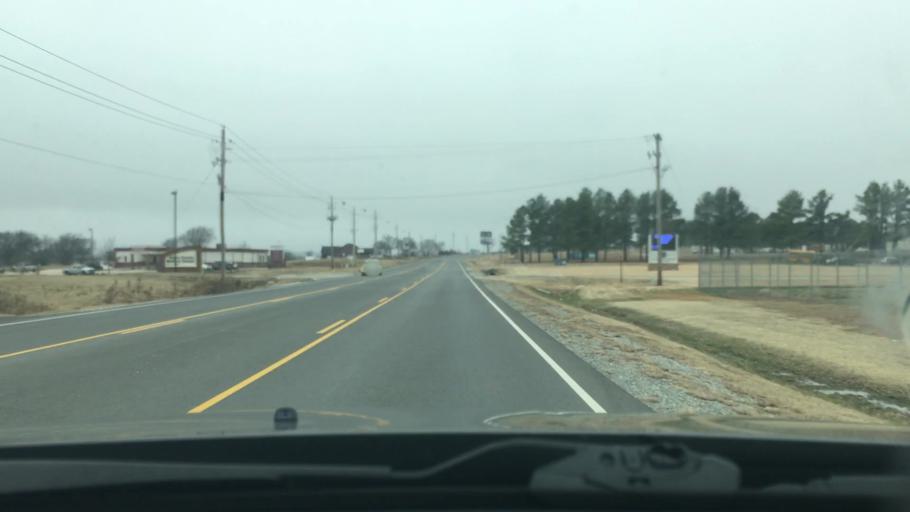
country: US
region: Oklahoma
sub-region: Atoka County
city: Atoka
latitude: 34.3941
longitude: -96.1495
